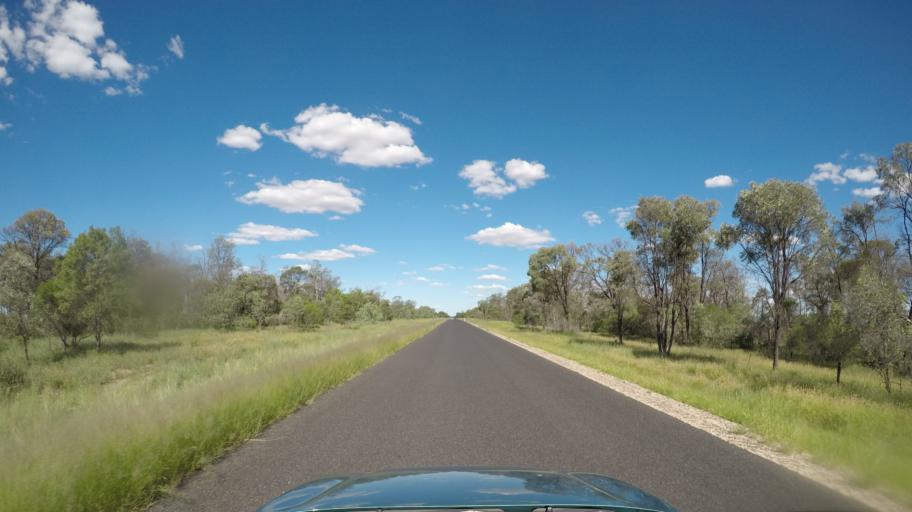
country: AU
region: Queensland
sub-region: Goondiwindi
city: Goondiwindi
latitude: -28.1678
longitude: 150.1924
